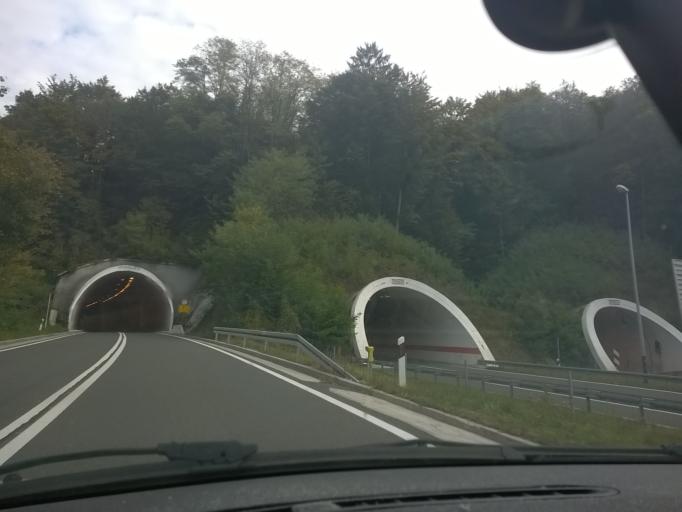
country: SI
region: Zetale
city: Zetale
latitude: 46.2469
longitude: 15.8497
